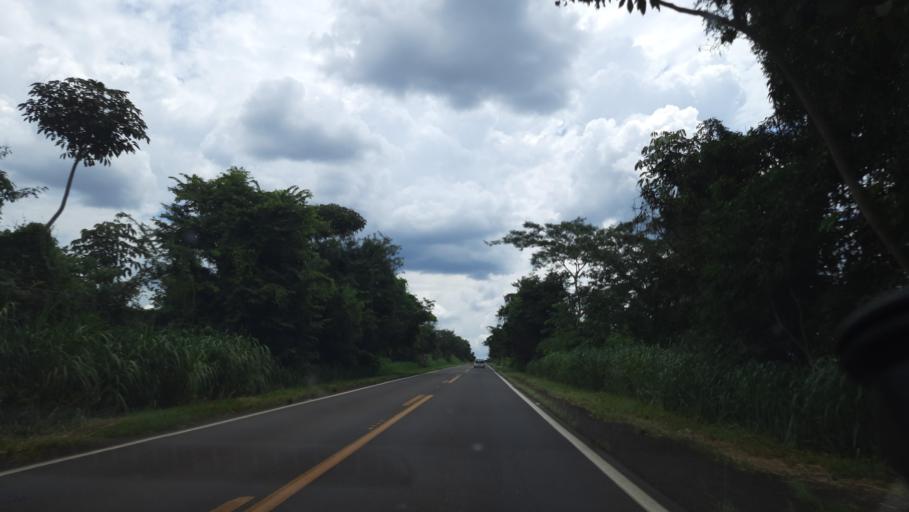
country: BR
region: Sao Paulo
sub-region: Mococa
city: Mococa
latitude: -21.4613
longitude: -47.1097
